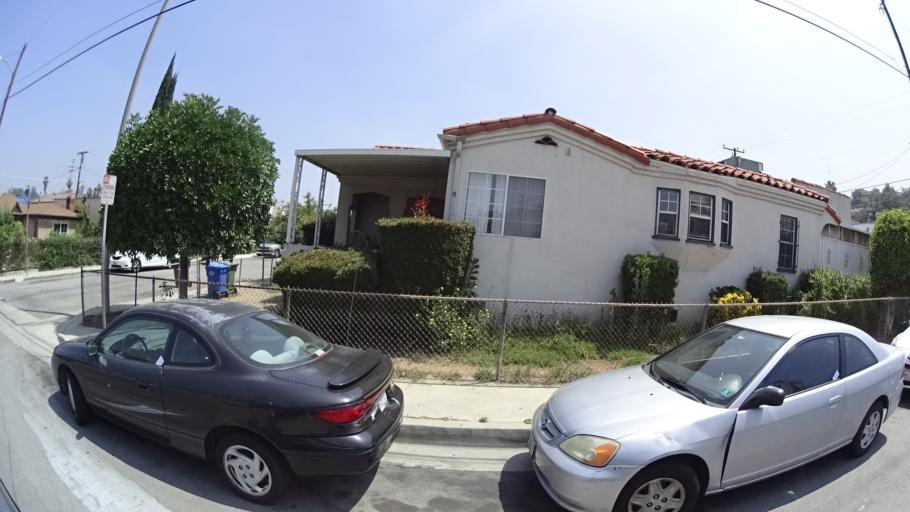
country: US
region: California
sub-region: Los Angeles County
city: Belvedere
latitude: 34.0567
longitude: -118.1769
